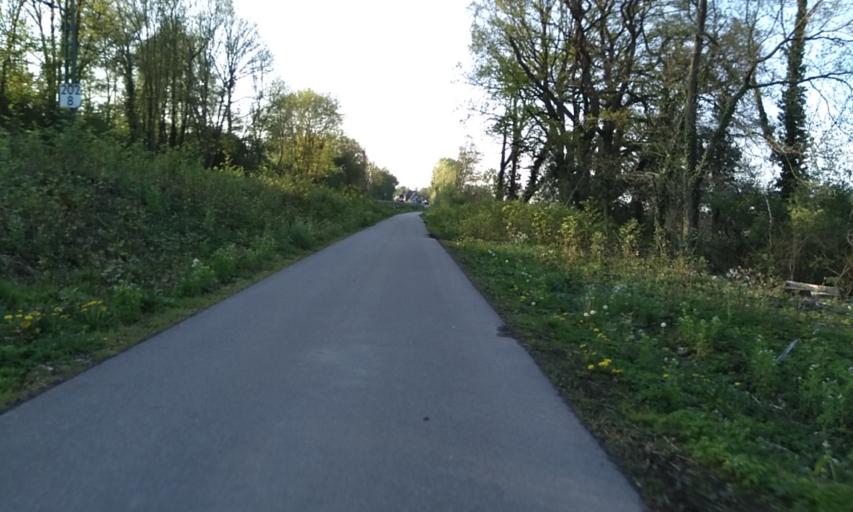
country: DE
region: Lower Saxony
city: Dollern
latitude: 53.5411
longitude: 9.5612
